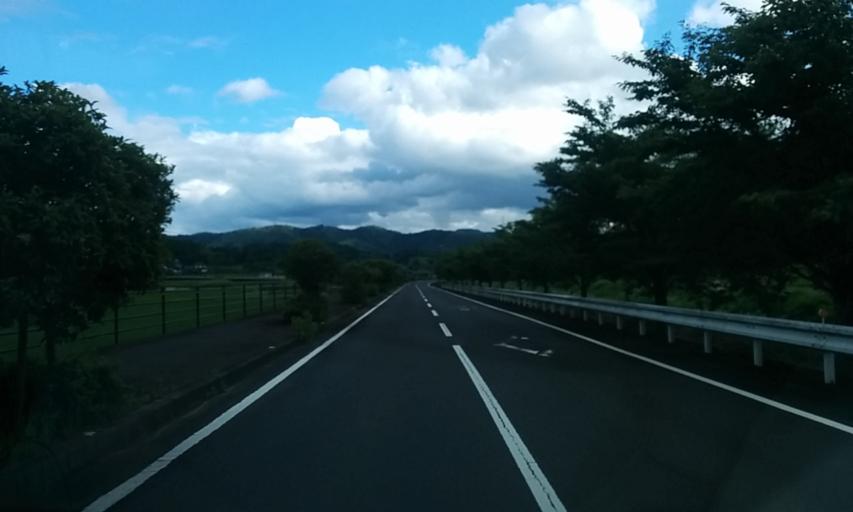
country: JP
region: Kyoto
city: Ayabe
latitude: 35.3448
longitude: 135.2888
